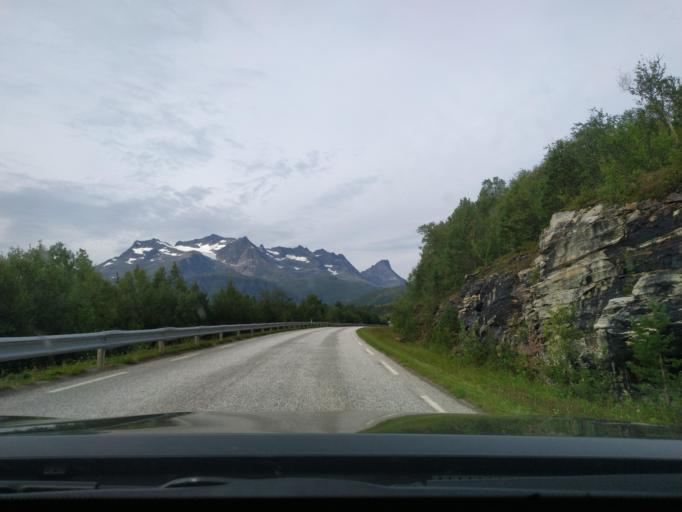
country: NO
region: Troms
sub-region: Dyroy
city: Brostadbotn
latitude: 68.9119
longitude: 17.5440
